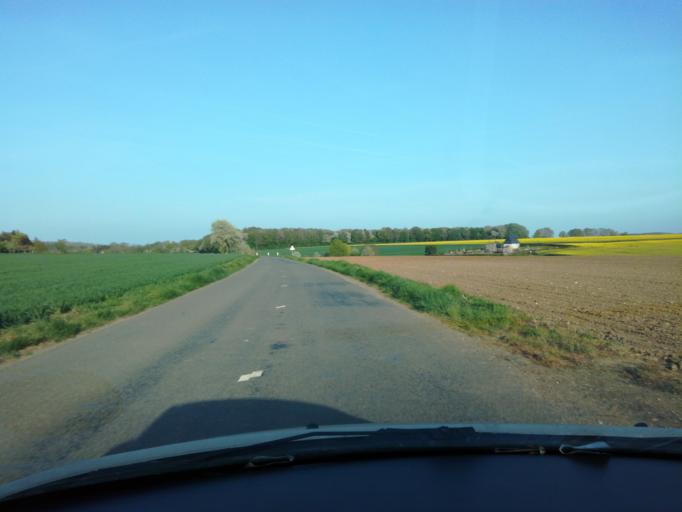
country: FR
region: Picardie
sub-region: Departement de la Somme
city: Poix-de-Picardie
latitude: 49.8161
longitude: 1.9903
